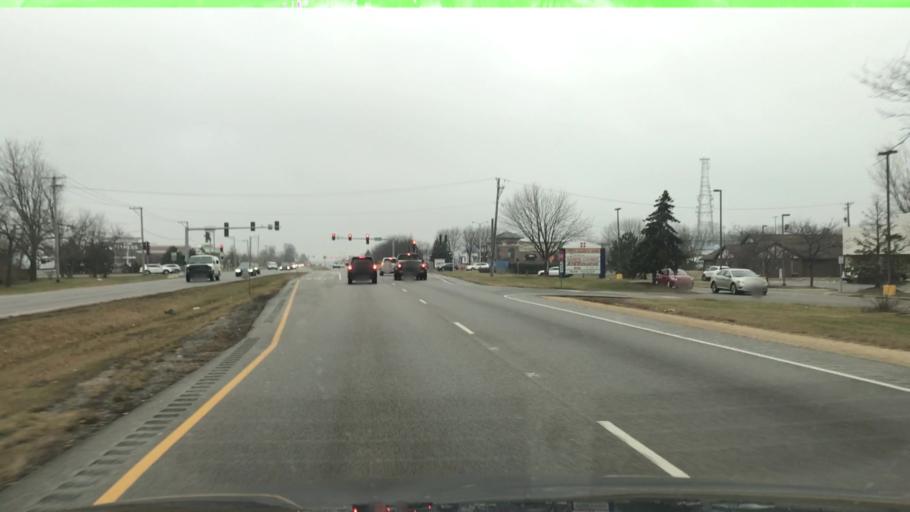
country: US
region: Illinois
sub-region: Lake County
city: Lake Zurich
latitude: 42.1832
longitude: -88.0855
